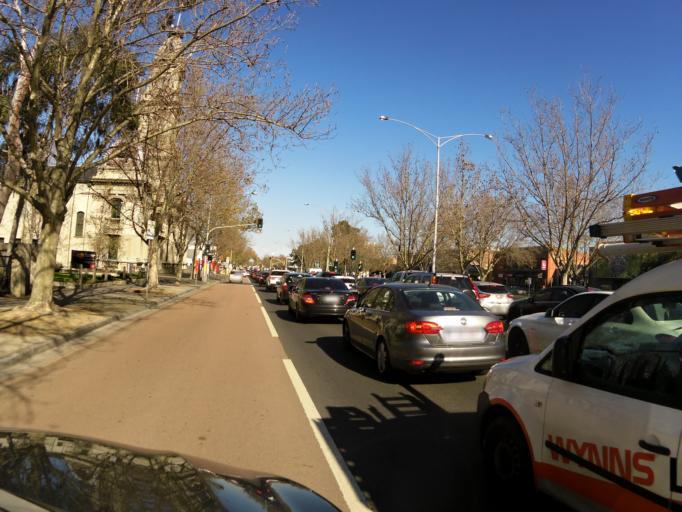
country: AU
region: Victoria
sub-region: Yarra
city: Clifton Hill
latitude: -37.8032
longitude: 144.9926
